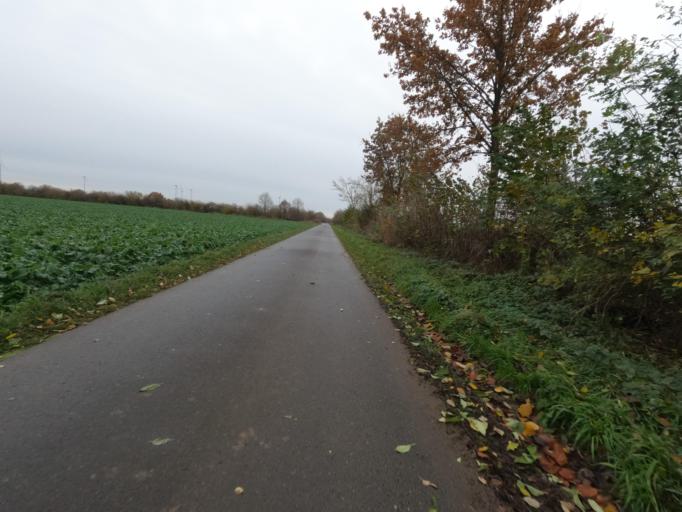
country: DE
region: North Rhine-Westphalia
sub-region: Regierungsbezirk Koln
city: Heinsberg
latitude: 51.0274
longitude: 6.1267
